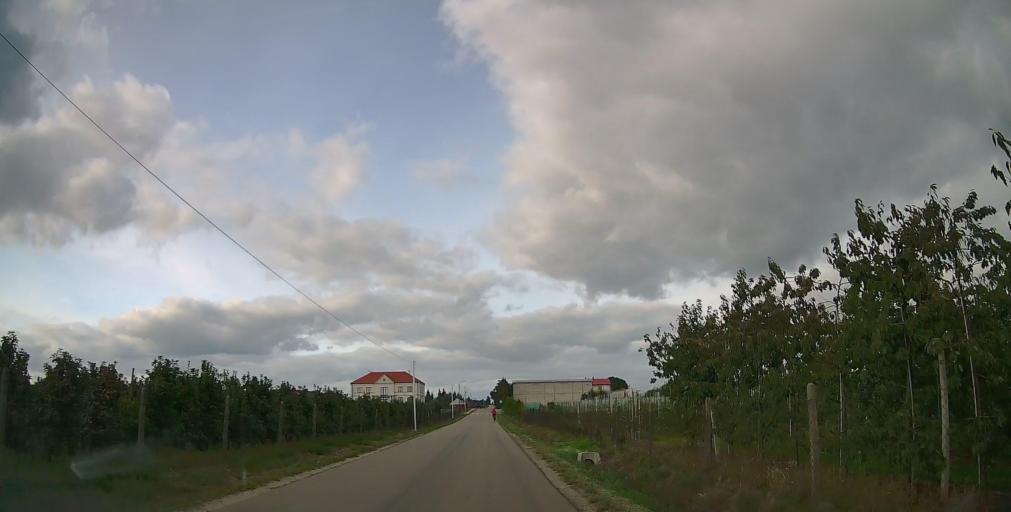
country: PL
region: Masovian Voivodeship
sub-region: Powiat bialobrzeski
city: Promna
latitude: 51.7095
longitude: 20.9581
